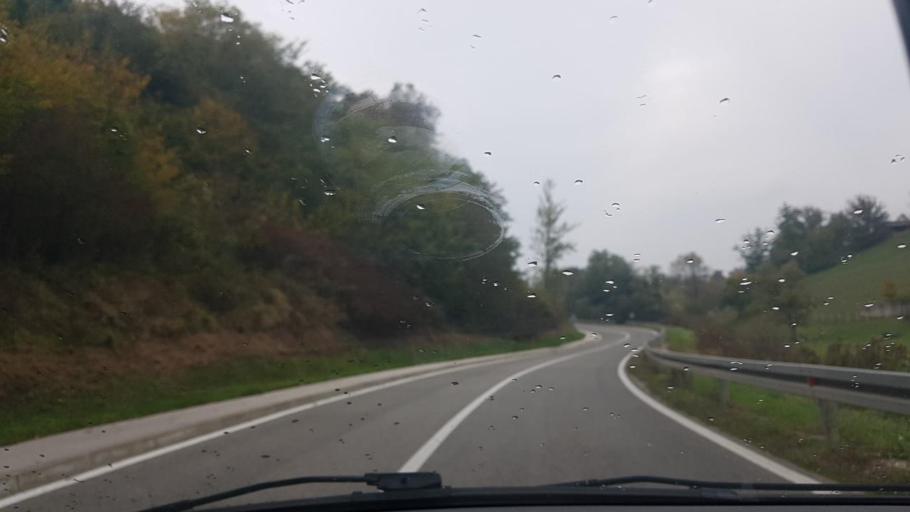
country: SI
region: Rogatec
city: Rogatec
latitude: 46.2040
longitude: 15.6931
